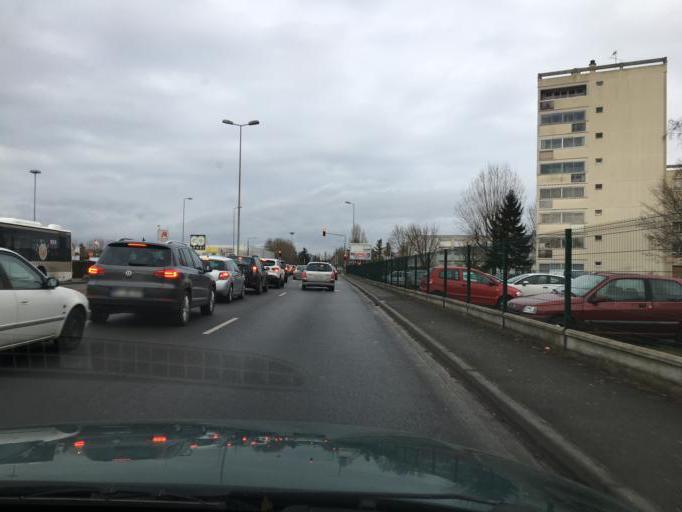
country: FR
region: Centre
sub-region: Departement du Loiret
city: Saint-Jean-de-la-Ruelle
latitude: 47.9037
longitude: 1.8639
